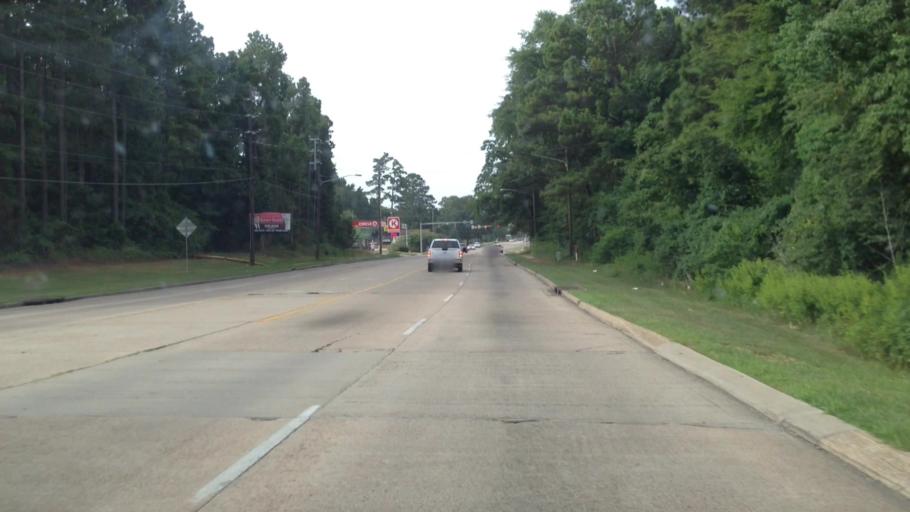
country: US
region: Louisiana
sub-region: Caddo Parish
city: Shreveport
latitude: 32.4145
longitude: -93.8148
